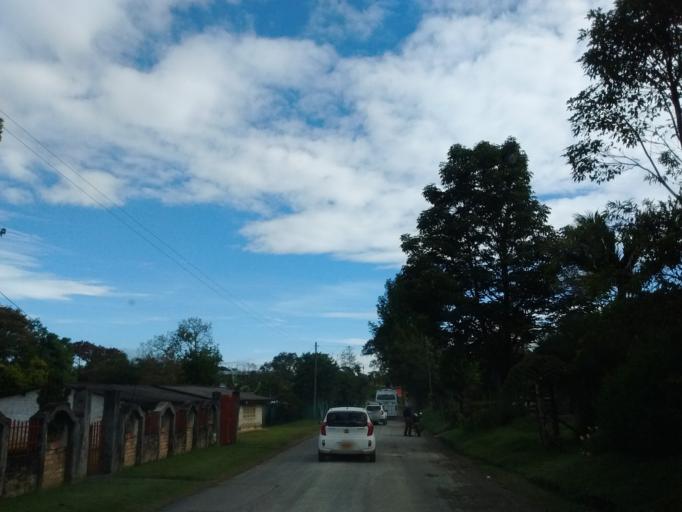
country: CO
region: Cauca
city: Cajibio
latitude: 2.6007
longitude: -76.5276
